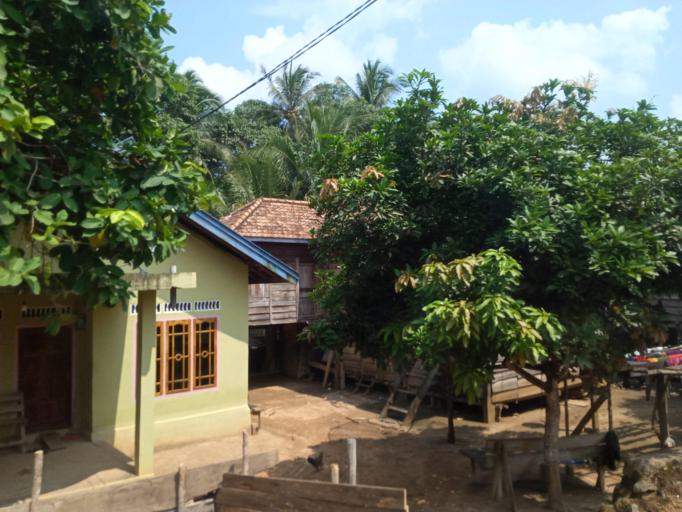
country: ID
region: Jambi
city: Mersam
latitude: -1.7068
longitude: 102.8844
